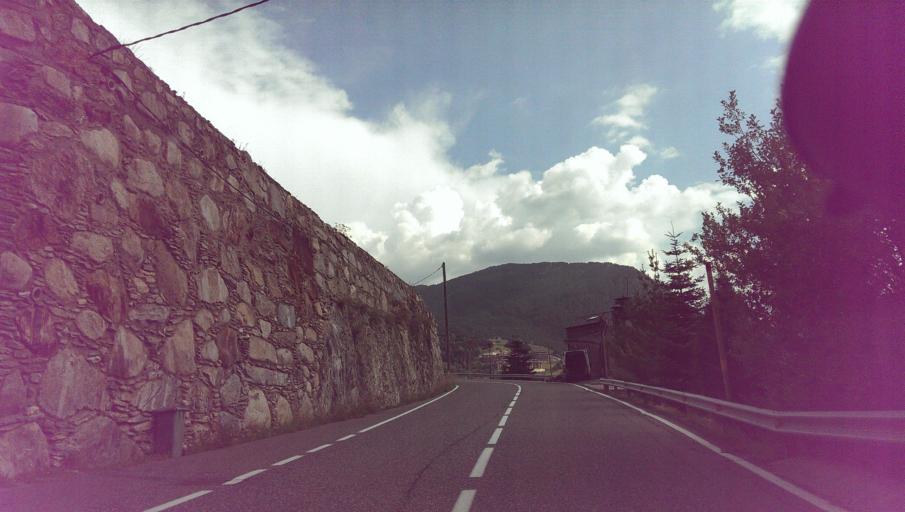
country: AD
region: Canillo
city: Canillo
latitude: 42.5695
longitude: 1.5984
